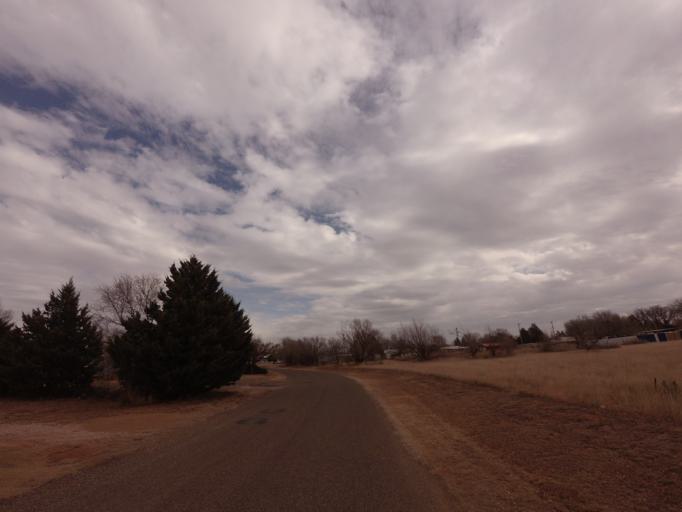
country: US
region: New Mexico
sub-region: Curry County
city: Clovis
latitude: 34.3812
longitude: -103.2028
